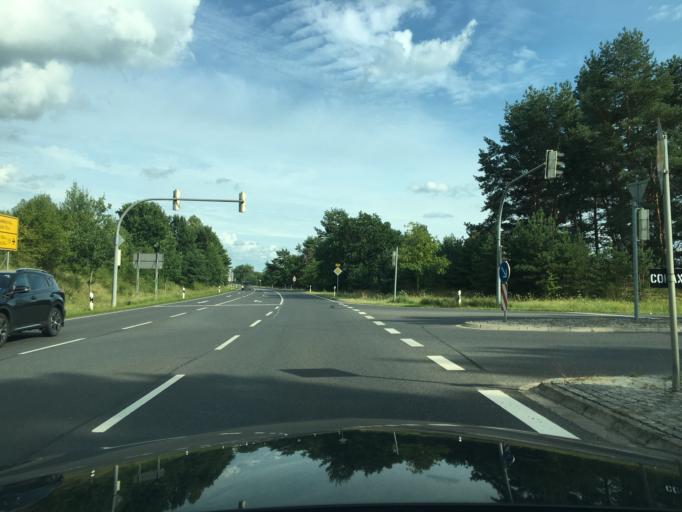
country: DE
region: Mecklenburg-Vorpommern
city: Neustrelitz
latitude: 53.3843
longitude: 13.0506
